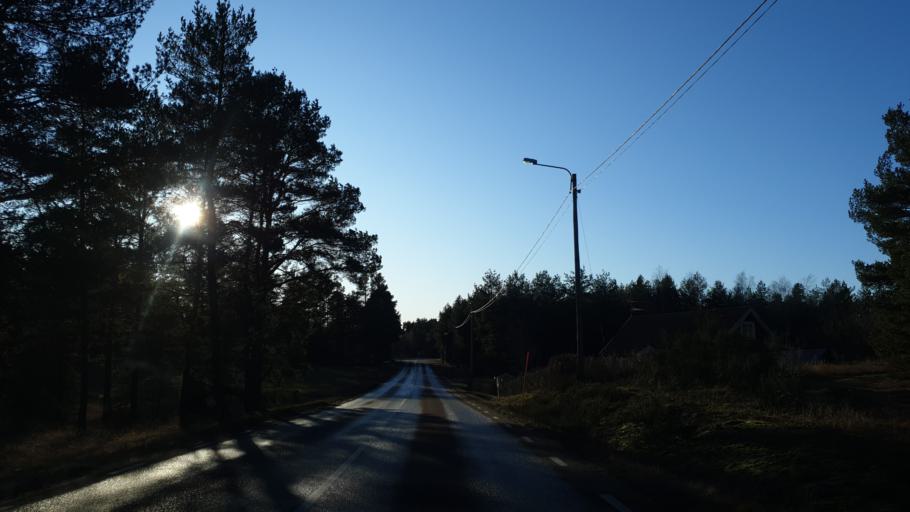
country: SE
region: Blekinge
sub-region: Ronneby Kommun
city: Kallinge
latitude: 56.2021
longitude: 15.3770
